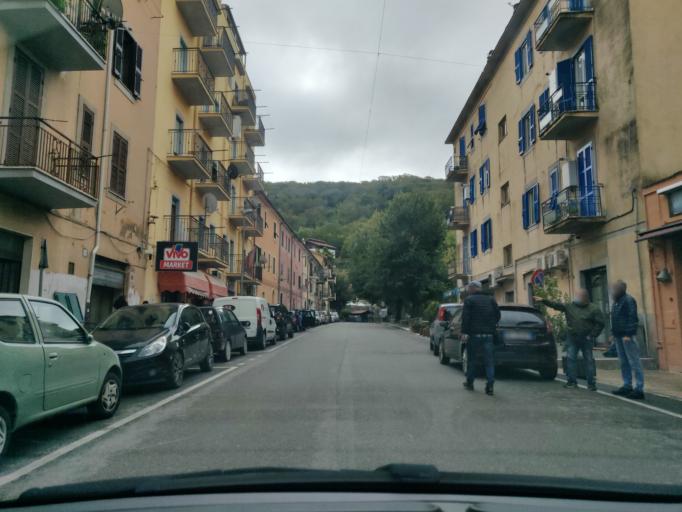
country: IT
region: Latium
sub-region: Citta metropolitana di Roma Capitale
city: Allumiere
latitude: 42.1547
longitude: 11.9049
